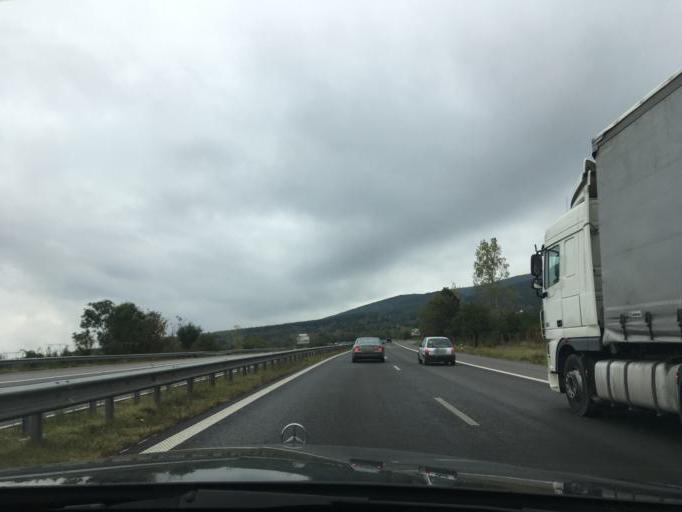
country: BG
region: Sofiya
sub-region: Obshtina Elin Pelin
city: Elin Pelin
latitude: 42.6087
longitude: 23.5452
